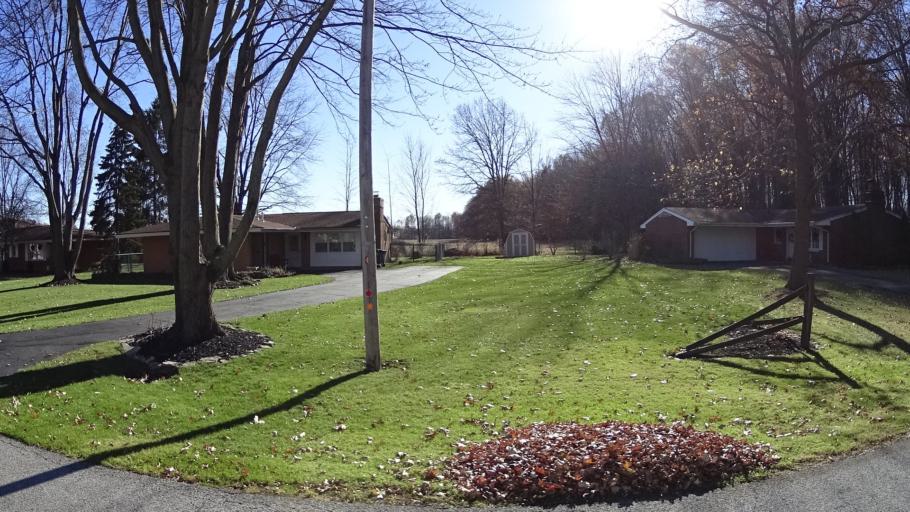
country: US
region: Ohio
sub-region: Lorain County
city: Avon Center
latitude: 41.4344
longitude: -81.9931
